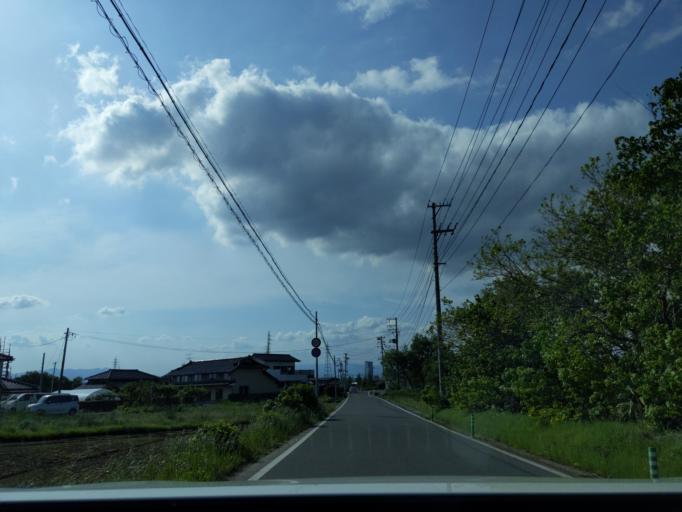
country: JP
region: Fukushima
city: Koriyama
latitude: 37.3775
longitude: 140.4103
